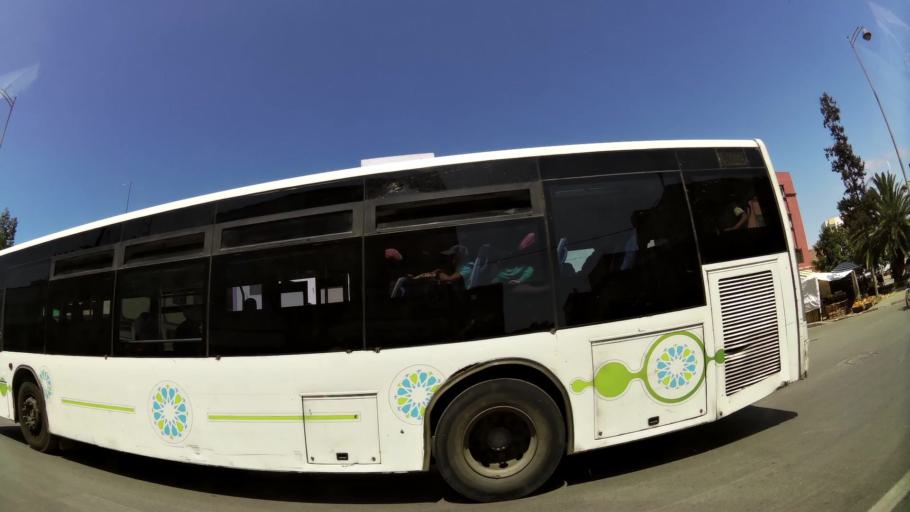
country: MA
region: Gharb-Chrarda-Beni Hssen
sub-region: Kenitra Province
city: Kenitra
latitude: 34.2450
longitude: -6.5518
